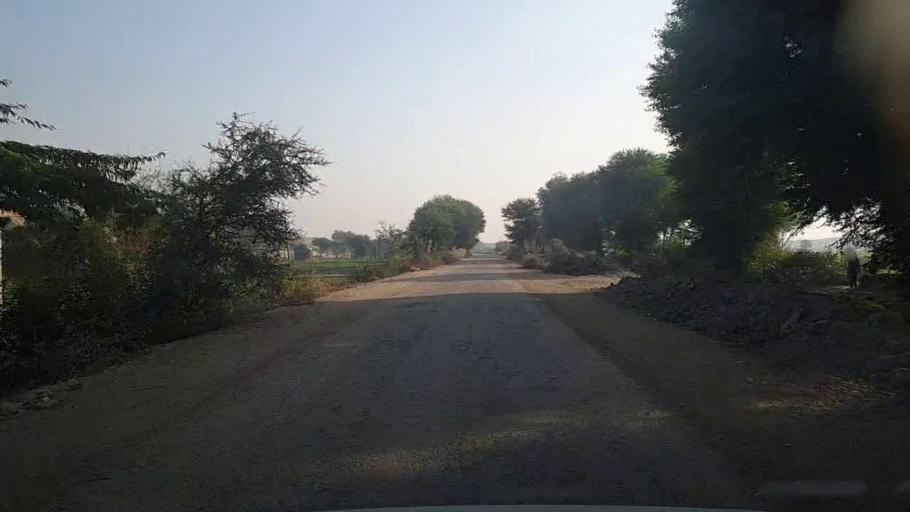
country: PK
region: Sindh
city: Karaundi
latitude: 26.7649
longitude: 68.4747
